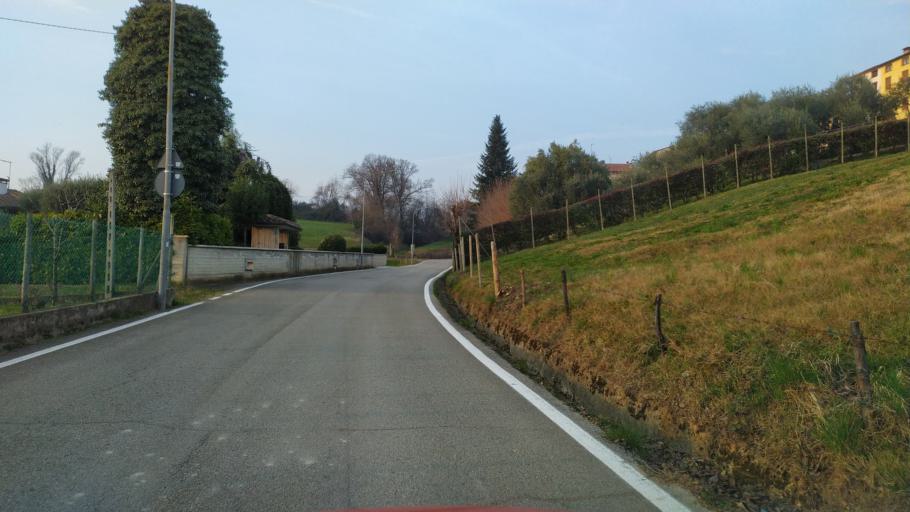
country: IT
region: Veneto
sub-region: Provincia di Vicenza
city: Sarcedo
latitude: 45.7028
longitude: 11.5244
